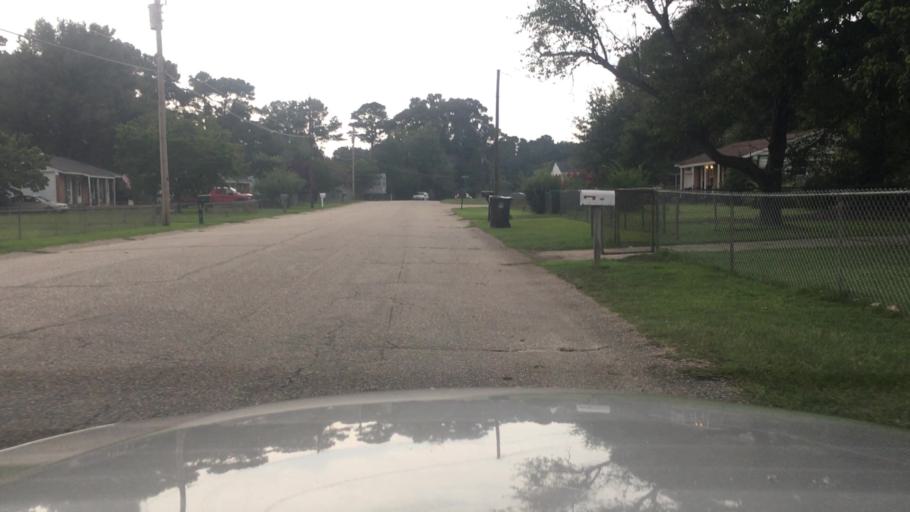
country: US
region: North Carolina
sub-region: Cumberland County
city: Fort Bragg
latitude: 35.0697
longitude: -79.0117
